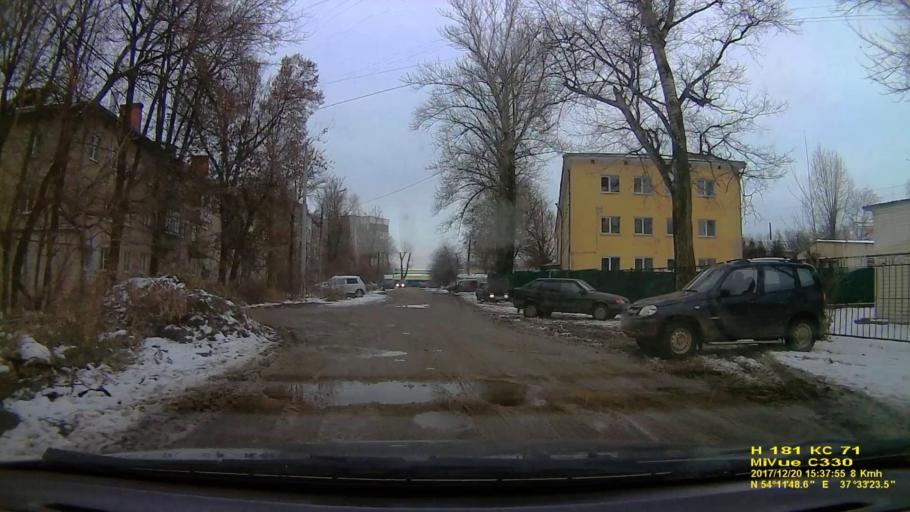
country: RU
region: Tula
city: Tula
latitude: 54.1968
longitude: 37.5565
